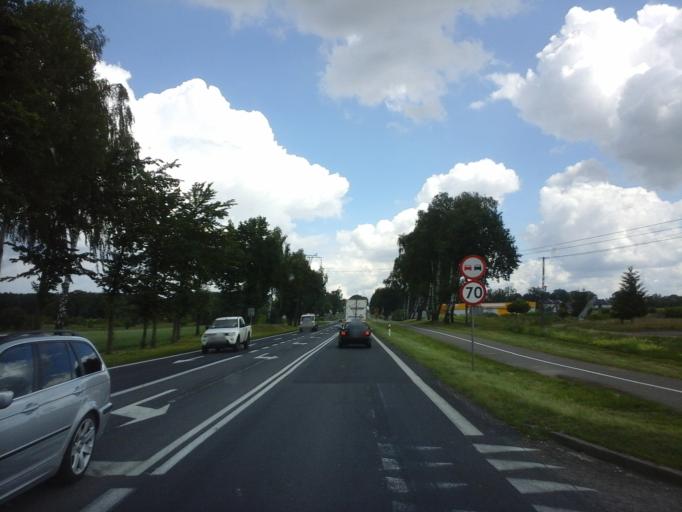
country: PL
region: West Pomeranian Voivodeship
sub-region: Koszalin
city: Koszalin
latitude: 54.1649
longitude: 16.0920
